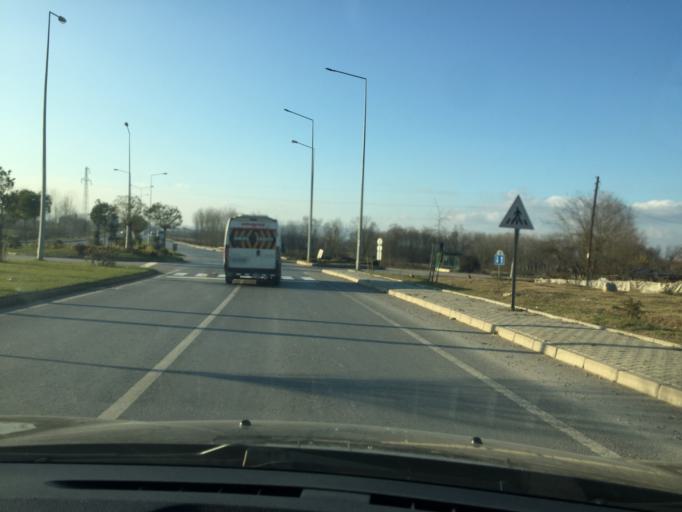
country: TR
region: Sakarya
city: Sogutlu
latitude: 40.9019
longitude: 30.5027
